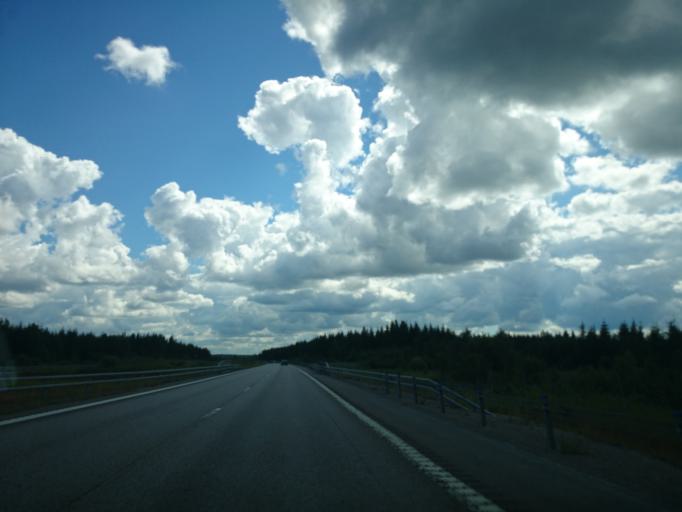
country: SE
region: Uppsala
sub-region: Tierps Kommun
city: Tierp
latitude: 60.4208
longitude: 17.4421
